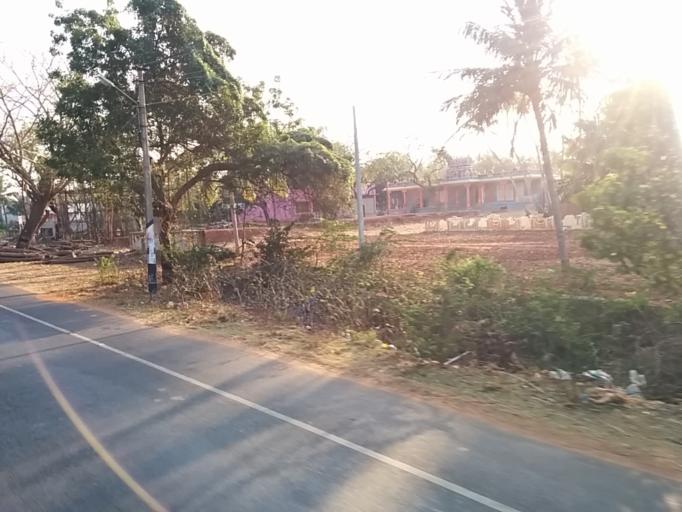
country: IN
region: Tamil Nadu
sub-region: Villupuram
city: Auroville
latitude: 11.9960
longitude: 79.8516
